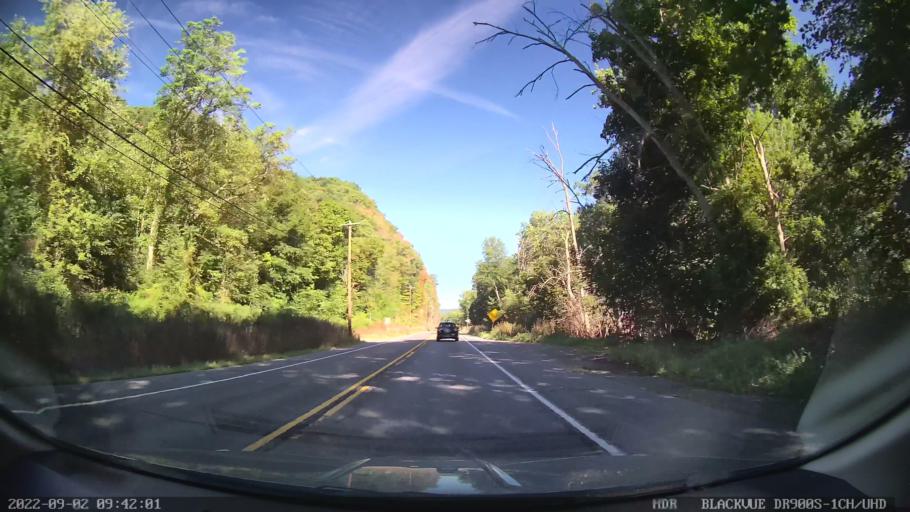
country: US
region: Pennsylvania
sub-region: Montour County
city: Danville
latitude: 40.9416
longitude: -76.6054
